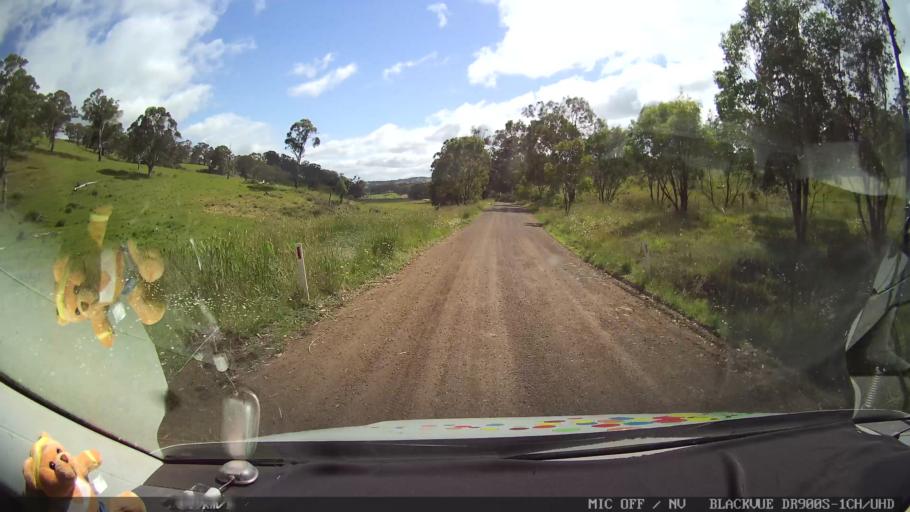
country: AU
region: New South Wales
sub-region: Guyra
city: Guyra
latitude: -29.9983
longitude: 151.6766
